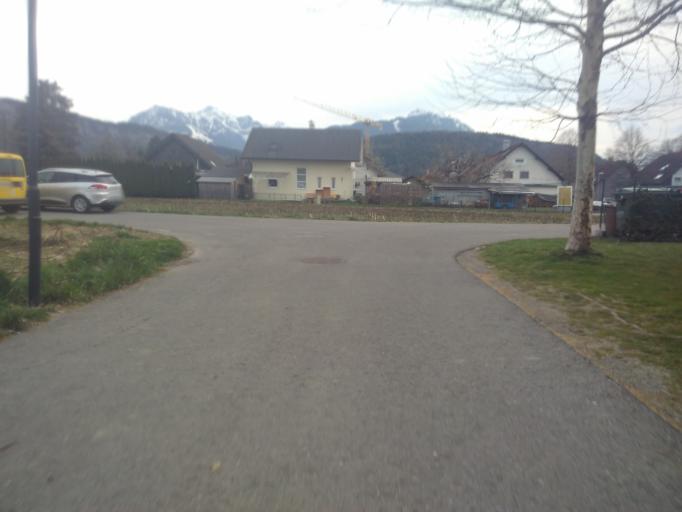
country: AT
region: Vorarlberg
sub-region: Politischer Bezirk Feldkirch
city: Rankweil
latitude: 47.2686
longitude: 9.6131
